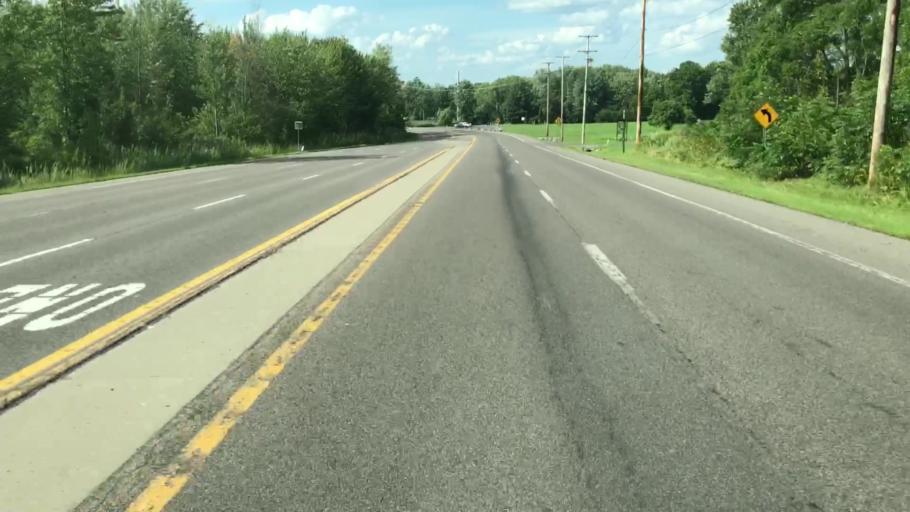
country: US
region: New York
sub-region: Onondaga County
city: Liverpool
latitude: 43.1499
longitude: -76.1882
